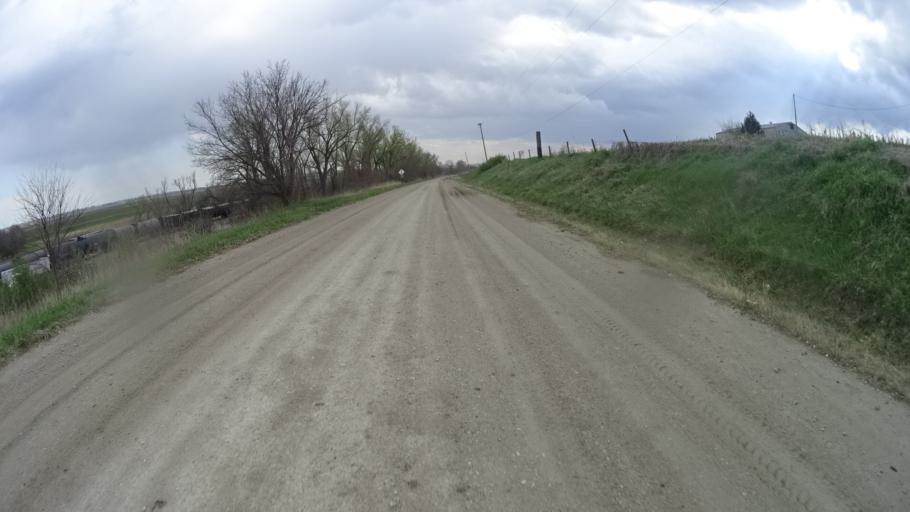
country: US
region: Nebraska
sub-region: Sarpy County
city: Offutt Air Force Base
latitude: 41.0969
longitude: -95.9133
